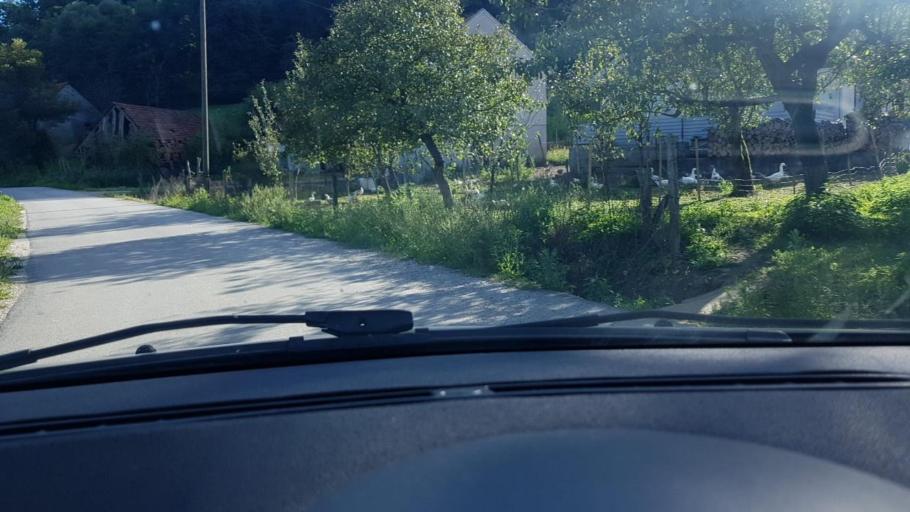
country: HR
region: Krapinsko-Zagorska
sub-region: Grad Krapina
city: Krapina
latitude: 46.1402
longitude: 15.8357
